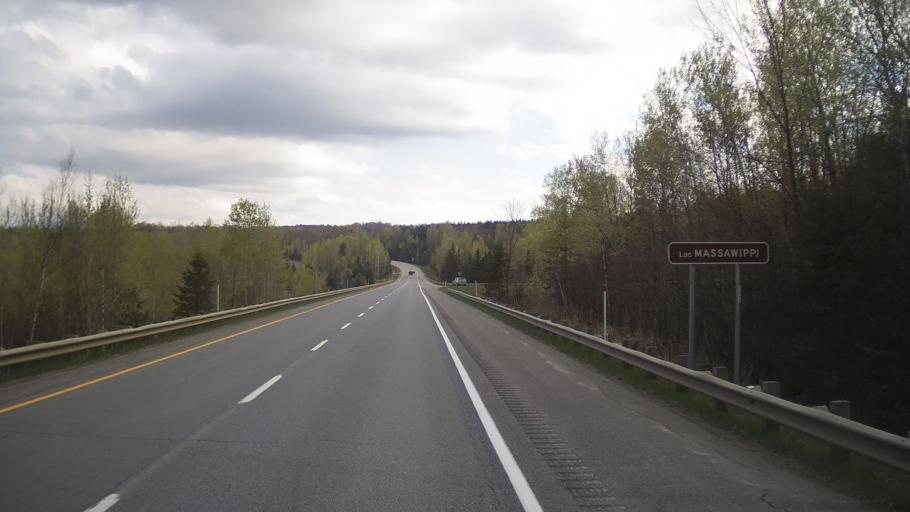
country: CA
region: Quebec
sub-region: Estrie
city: Magog
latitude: 45.1811
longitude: -72.0736
